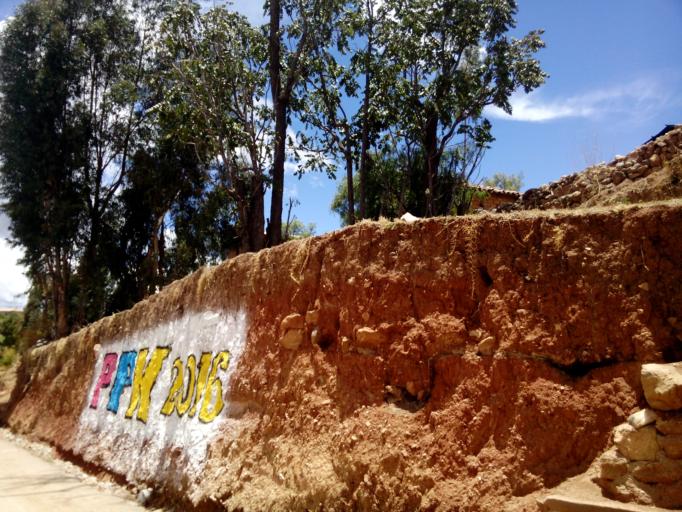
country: PE
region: Ayacucho
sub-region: Provincia de Victor Fajardo
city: Canaria
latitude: -13.8783
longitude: -73.9326
